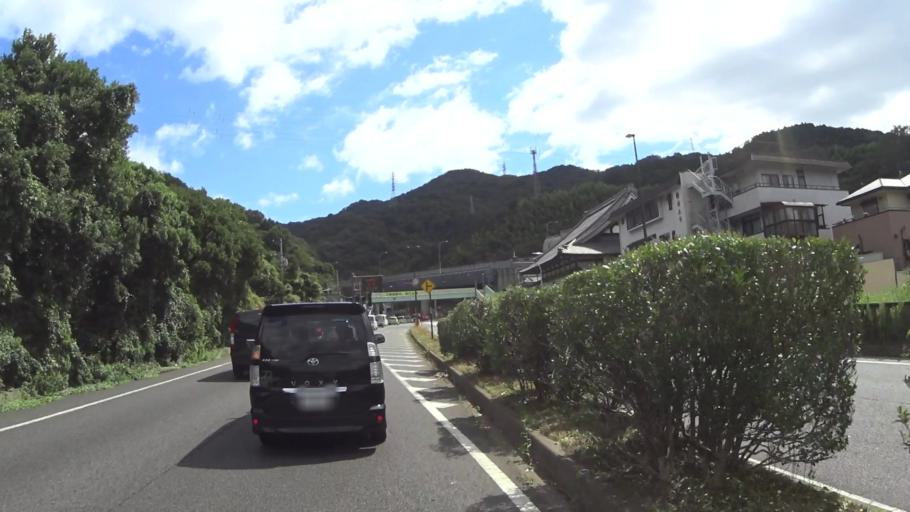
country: JP
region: Shiga Prefecture
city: Otsu-shi
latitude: 34.9909
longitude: 135.8387
